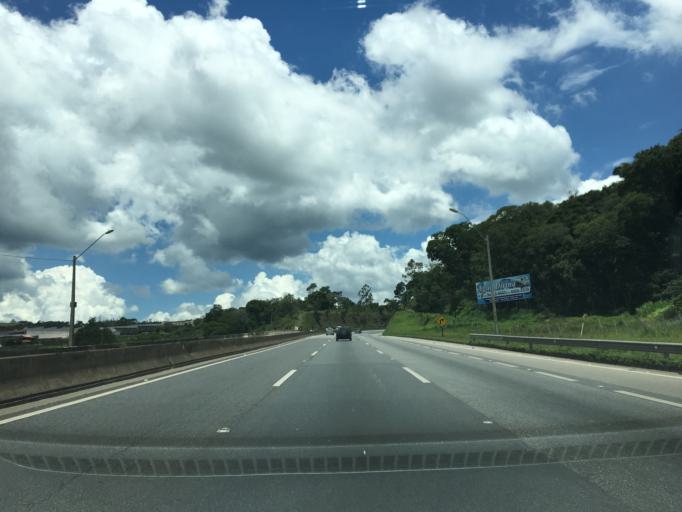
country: BR
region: Sao Paulo
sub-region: Mairipora
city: Mairipora
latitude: -23.2463
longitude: -46.5943
